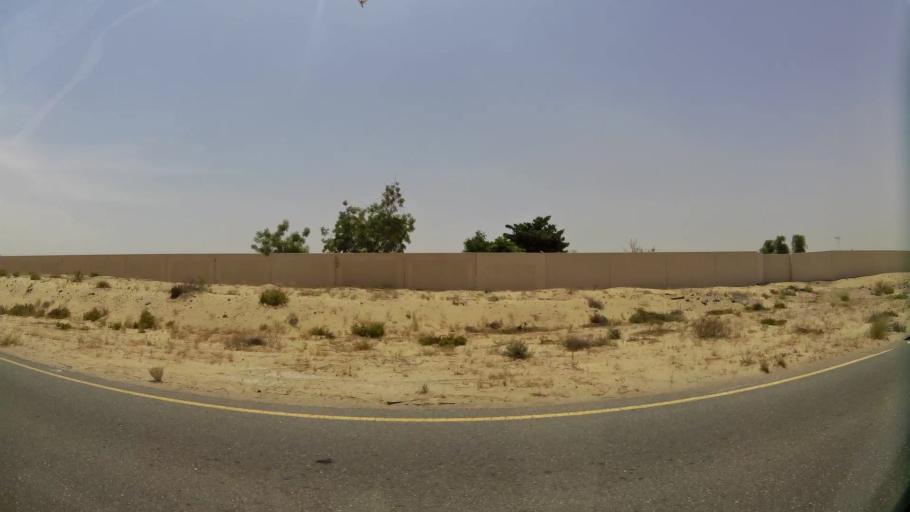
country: AE
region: Ash Shariqah
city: Sharjah
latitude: 25.2391
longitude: 55.4946
